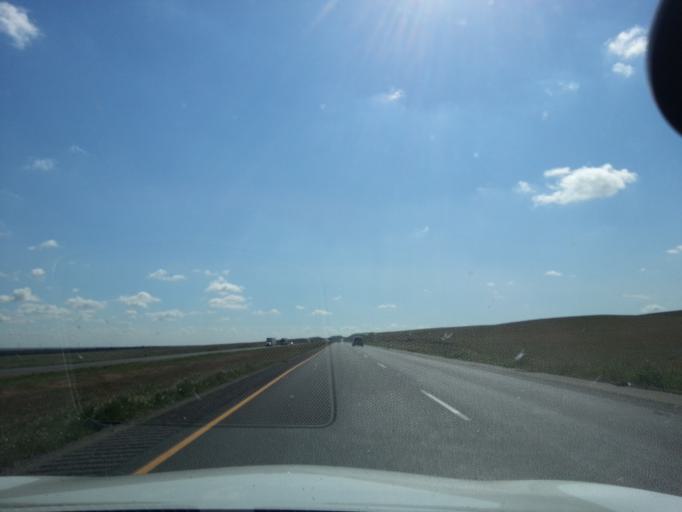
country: US
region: California
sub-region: Fresno County
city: Coalinga
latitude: 36.3416
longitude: -120.3102
